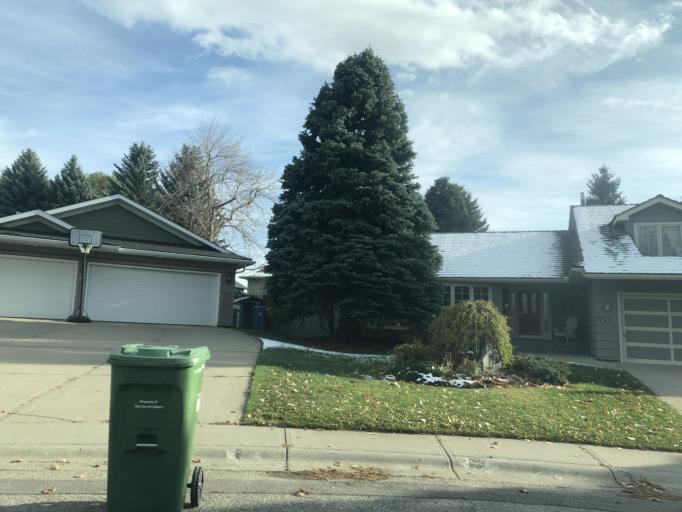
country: CA
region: Alberta
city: Calgary
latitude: 50.9345
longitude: -114.0587
